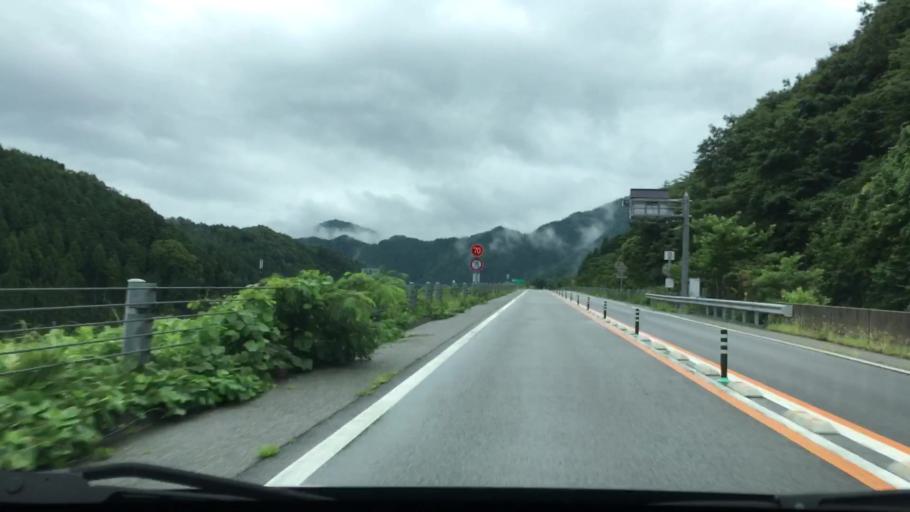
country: JP
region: Hyogo
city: Toyooka
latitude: 35.2489
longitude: 134.7911
